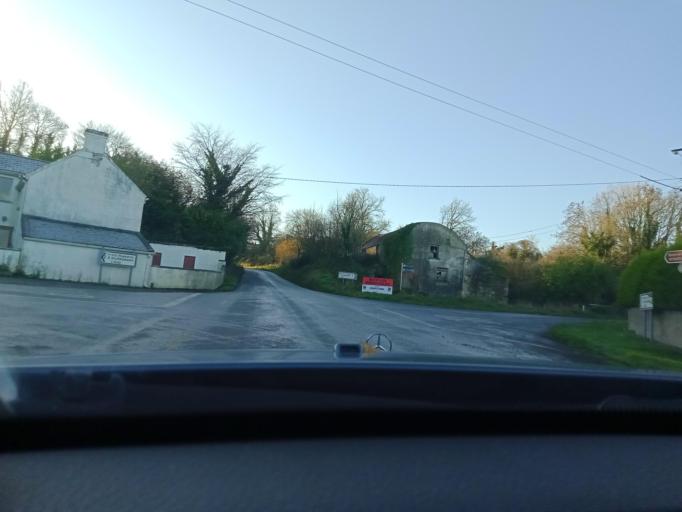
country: IE
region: Leinster
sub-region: Kilkenny
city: Callan
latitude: 52.4672
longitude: -7.3967
